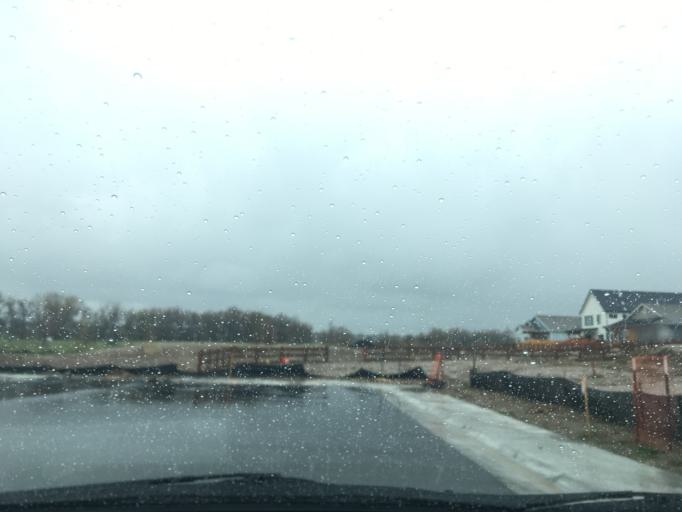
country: US
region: Colorado
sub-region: Boulder County
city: Lafayette
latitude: 39.9805
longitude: -105.0794
